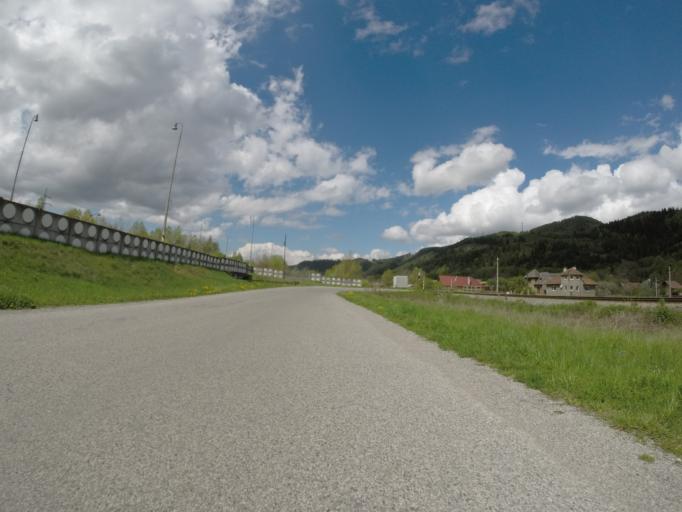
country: SK
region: Banskobystricky
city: Hrochot,Slovakia
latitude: 48.8150
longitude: 19.4328
